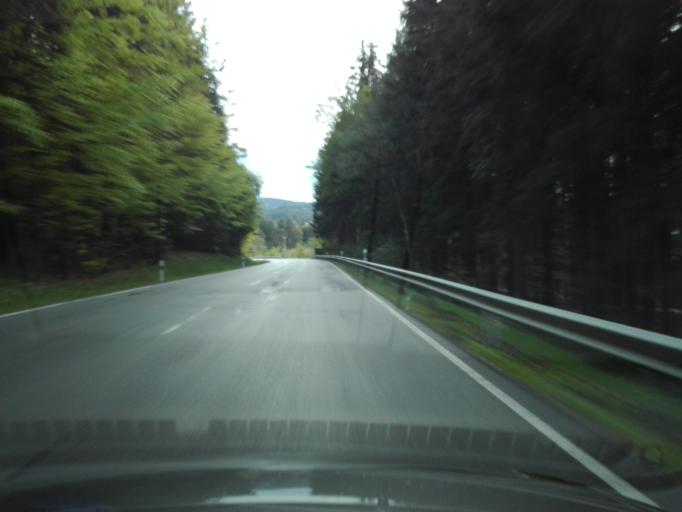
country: DE
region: Bavaria
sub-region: Lower Bavaria
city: Wegscheid
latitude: 48.5811
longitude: 13.7697
